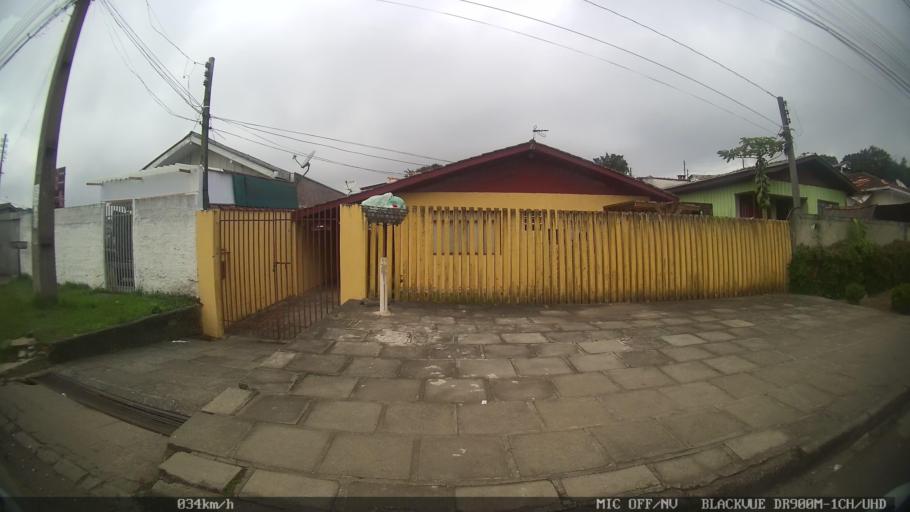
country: BR
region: Parana
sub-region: Curitiba
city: Curitiba
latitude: -25.3699
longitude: -49.2694
